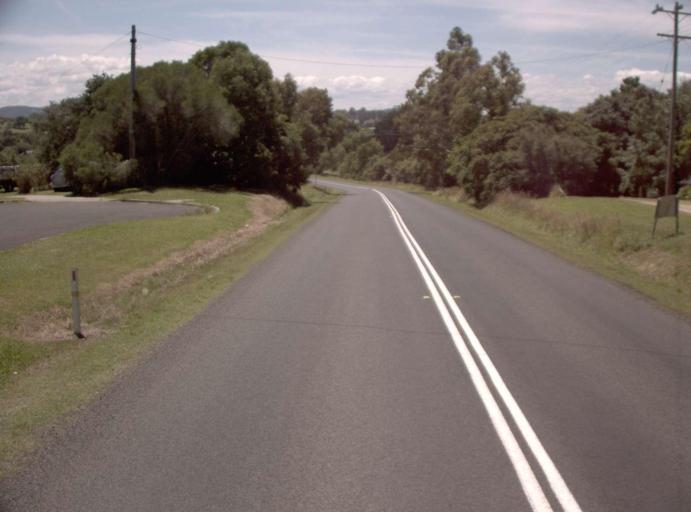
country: AU
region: Victoria
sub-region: Baw Baw
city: Warragul
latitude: -38.0092
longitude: 145.9557
